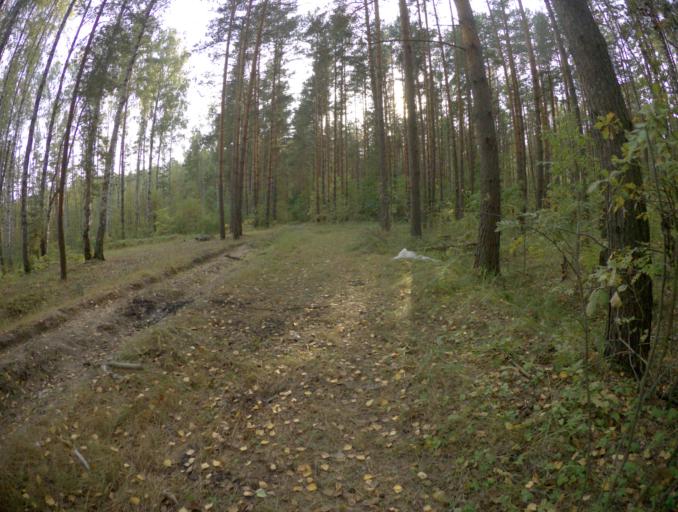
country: RU
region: Vladimir
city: Raduzhnyy
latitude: 56.0577
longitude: 40.3490
